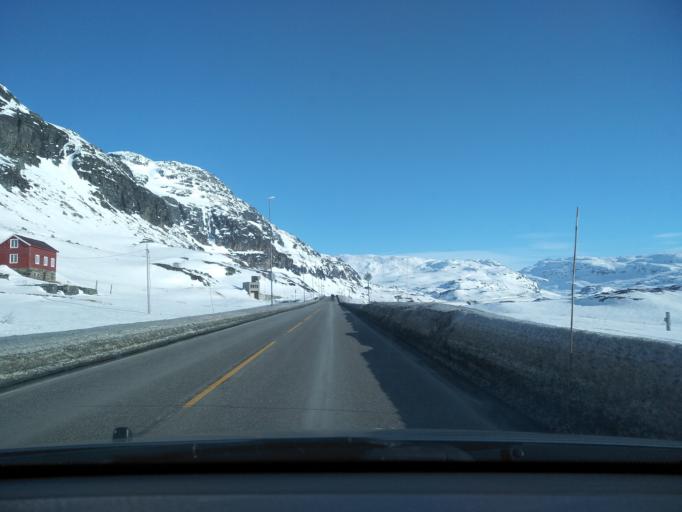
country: NO
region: Hordaland
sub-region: Odda
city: Odda
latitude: 59.8494
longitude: 6.9497
